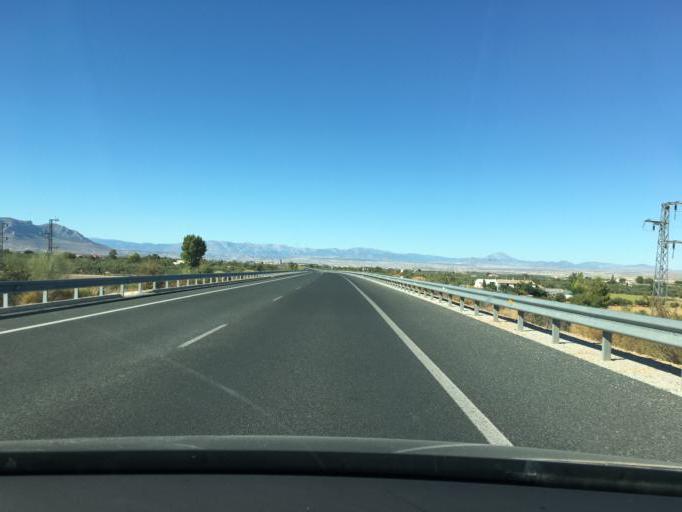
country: ES
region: Andalusia
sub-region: Provincia de Granada
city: Caniles
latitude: 37.4654
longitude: -2.7371
